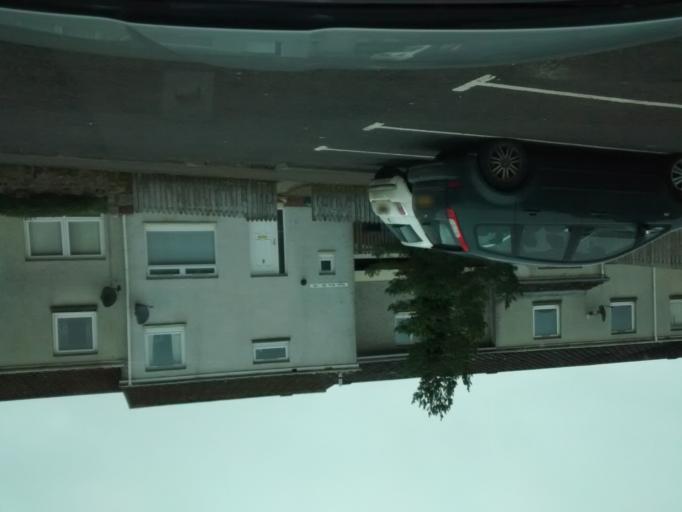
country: GB
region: Scotland
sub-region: West Lothian
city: Livingston
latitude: 55.8789
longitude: -3.5060
